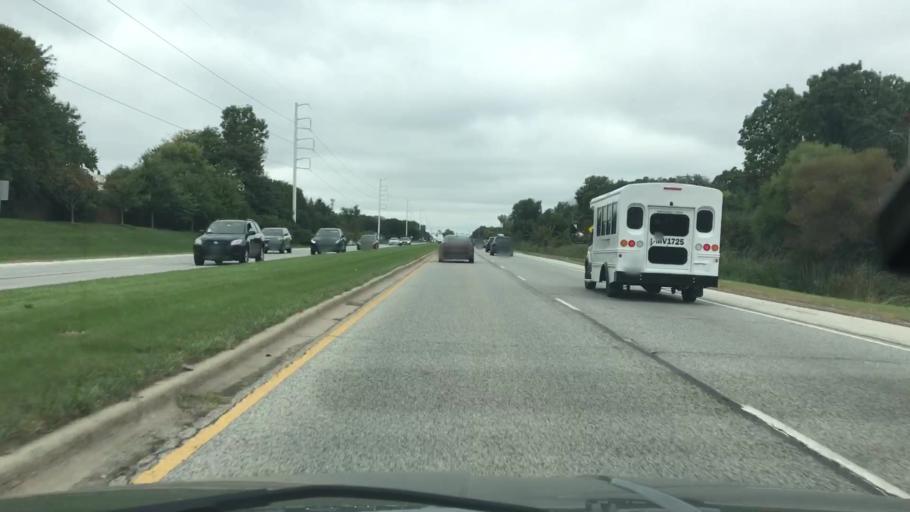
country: US
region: Illinois
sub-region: DuPage County
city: Woodridge
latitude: 41.7492
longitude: -88.0953
